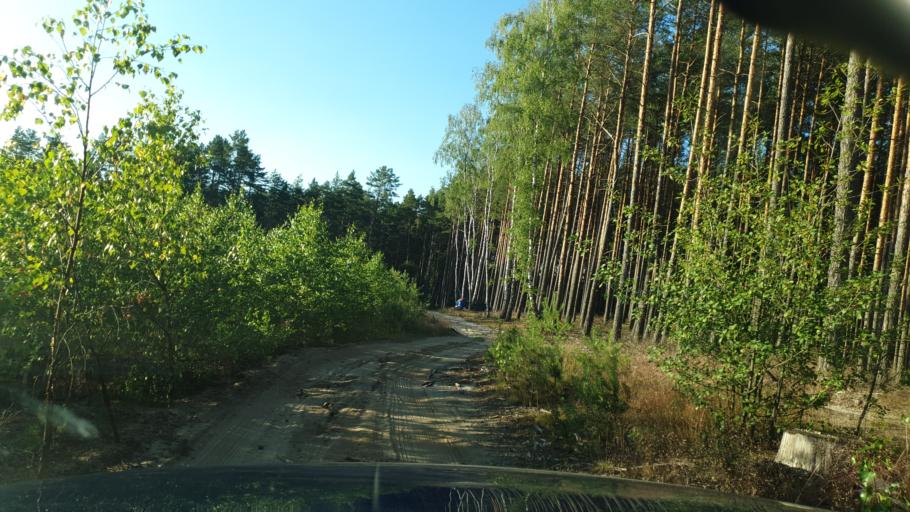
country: PL
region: Pomeranian Voivodeship
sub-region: Powiat bytowski
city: Lipnica
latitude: 53.8844
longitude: 17.4268
